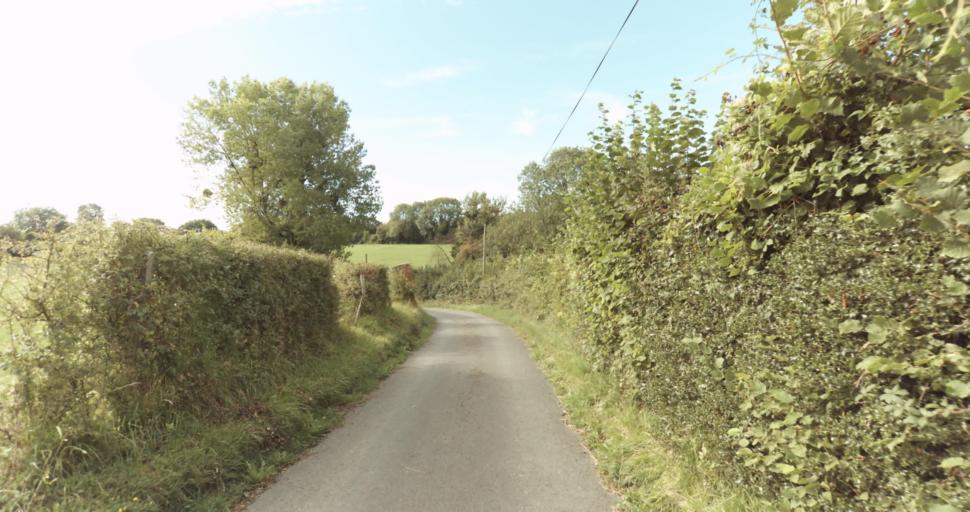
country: FR
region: Lower Normandy
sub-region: Departement de l'Orne
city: Gace
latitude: 48.8061
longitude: 0.2412
